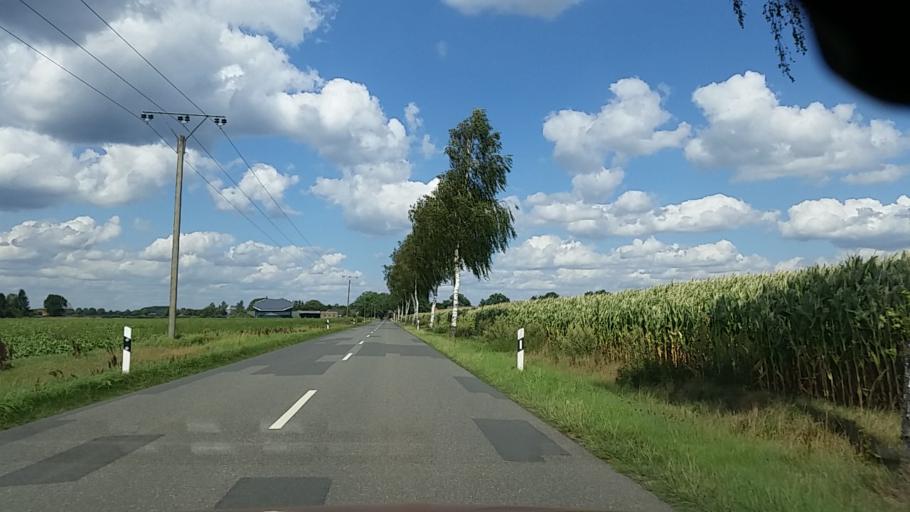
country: DE
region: Lower Saxony
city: Sprakensehl
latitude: 52.7457
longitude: 10.5148
